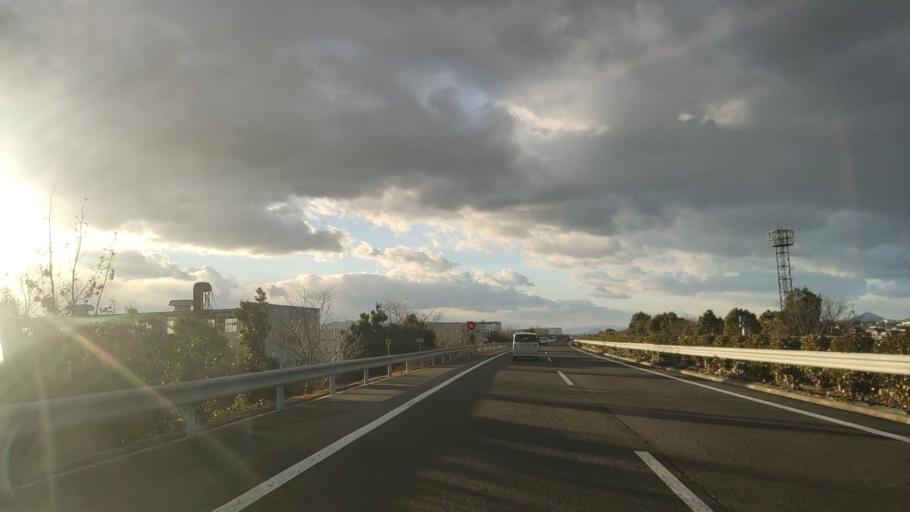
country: JP
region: Ehime
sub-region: Shikoku-chuo Shi
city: Matsuyama
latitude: 33.7849
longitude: 132.8466
